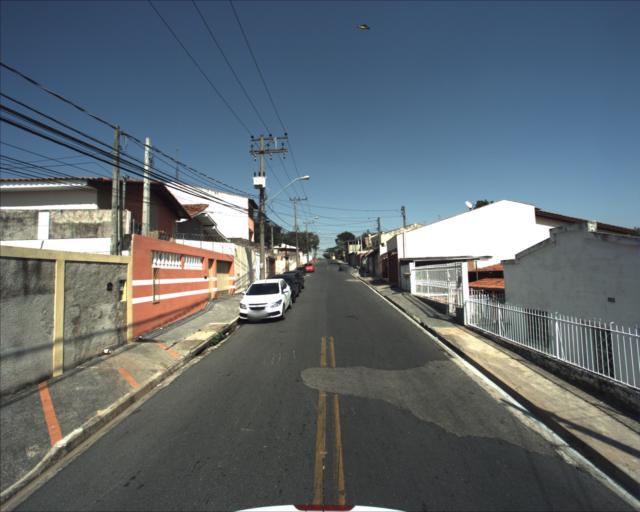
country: BR
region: Sao Paulo
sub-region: Sorocaba
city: Sorocaba
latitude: -23.4760
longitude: -47.4687
